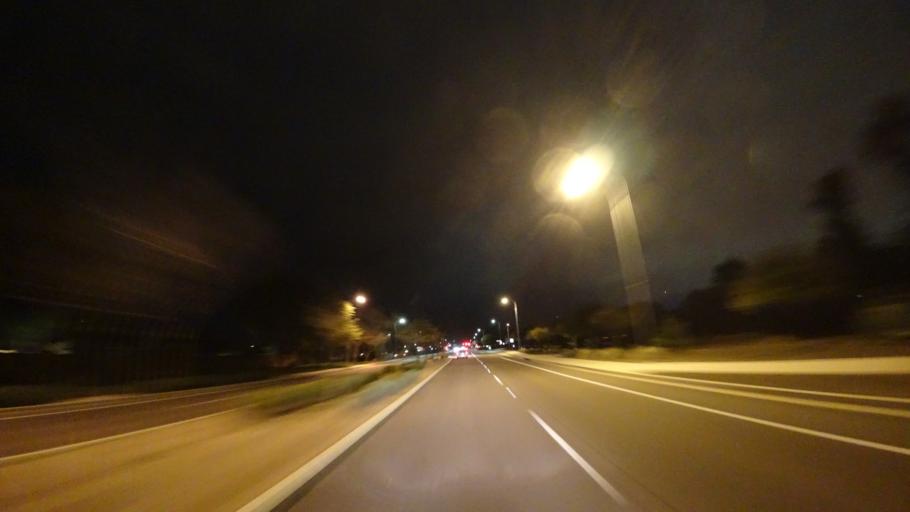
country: US
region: Arizona
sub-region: Maricopa County
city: Chandler
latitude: 33.2338
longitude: -111.7845
